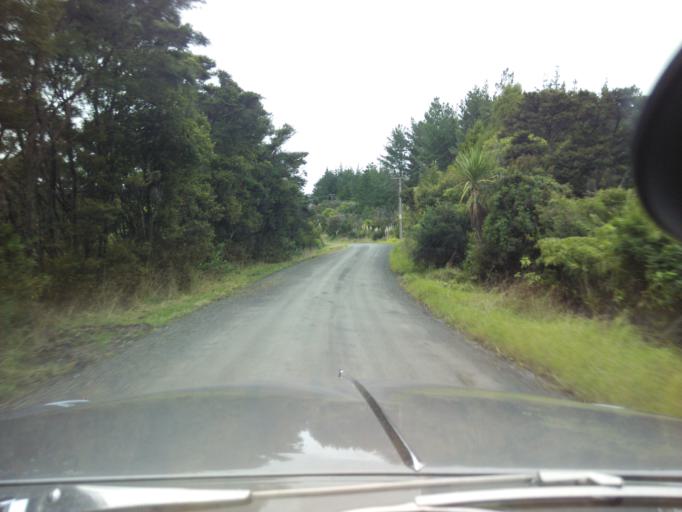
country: NZ
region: Auckland
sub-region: Auckland
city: Warkworth
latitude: -36.5354
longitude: 174.6162
